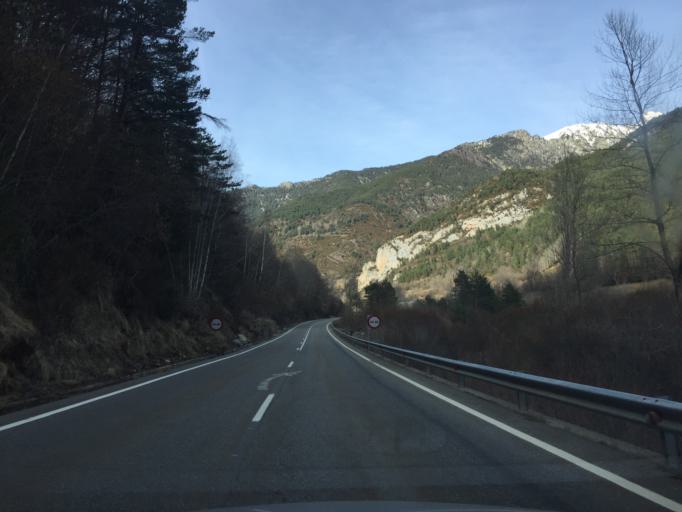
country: ES
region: Aragon
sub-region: Provincia de Huesca
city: Bielsa
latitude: 42.6172
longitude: 0.2307
